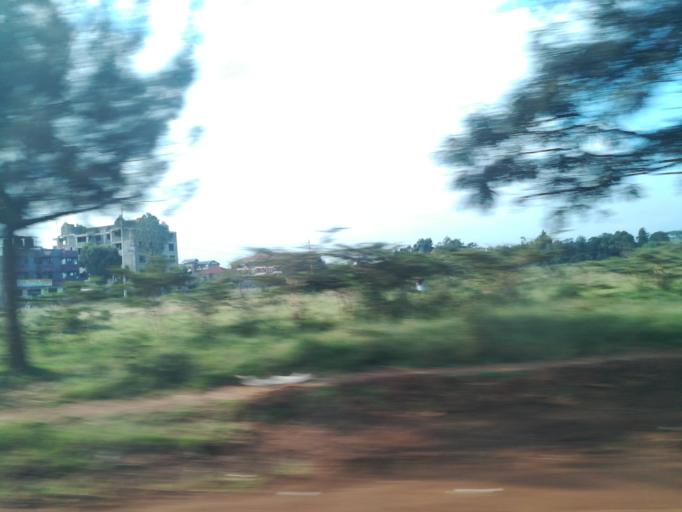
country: KE
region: Nairobi Area
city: Thika
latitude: -1.0430
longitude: 37.0586
